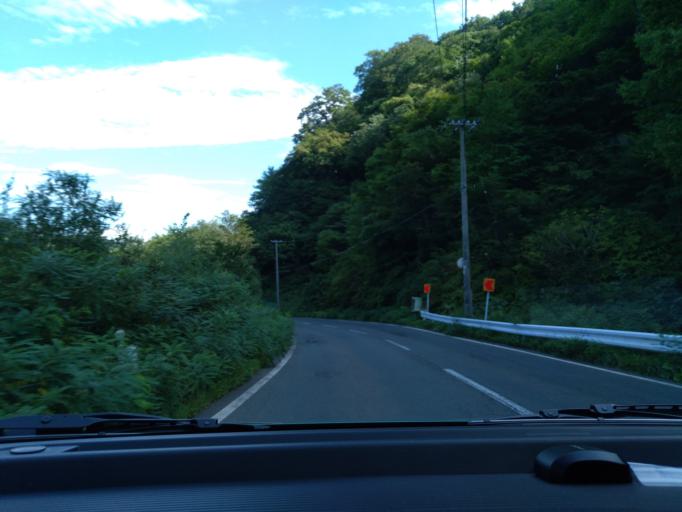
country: JP
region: Iwate
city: Shizukuishi
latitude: 39.6291
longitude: 141.0605
